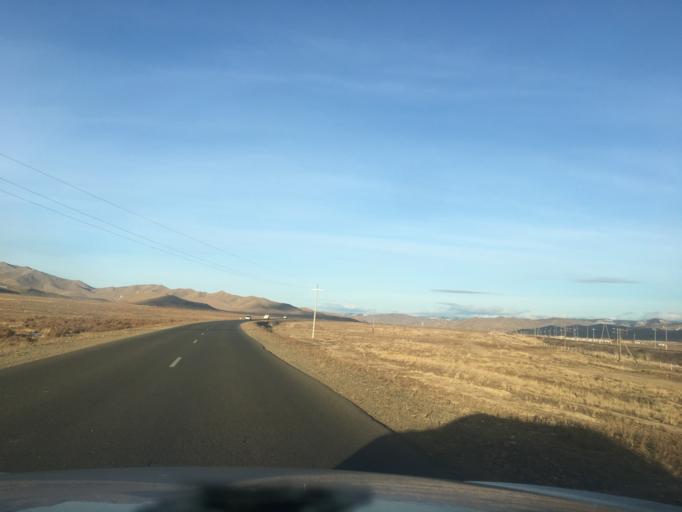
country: MN
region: Central Aimak
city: Ihsueuej
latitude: 48.0804
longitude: 106.5848
